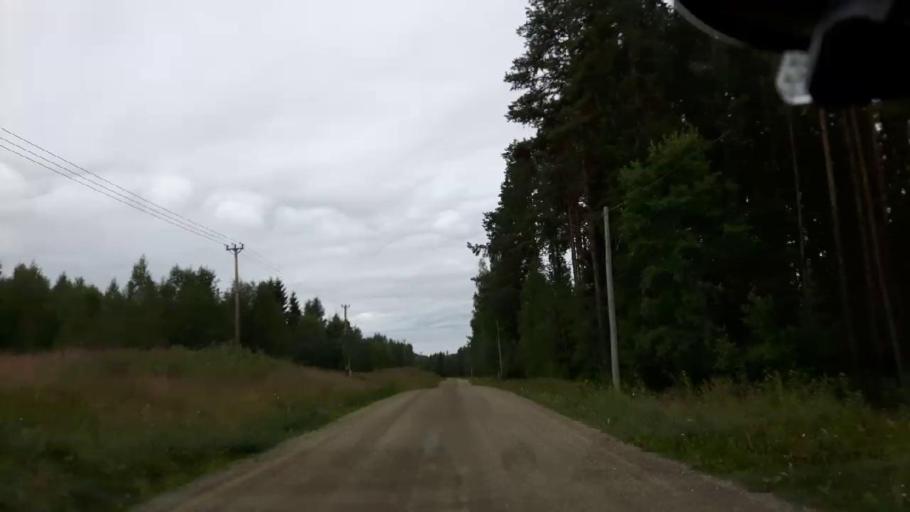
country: SE
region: Jaemtland
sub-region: Braecke Kommun
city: Braecke
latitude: 63.0233
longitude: 15.3728
